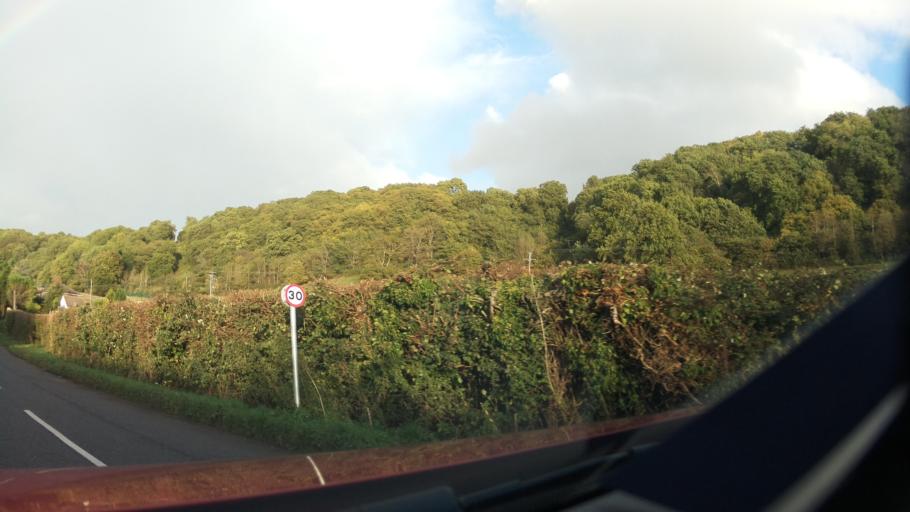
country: GB
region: England
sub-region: South Gloucestershire
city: Severn Beach
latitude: 51.5223
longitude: -2.6410
